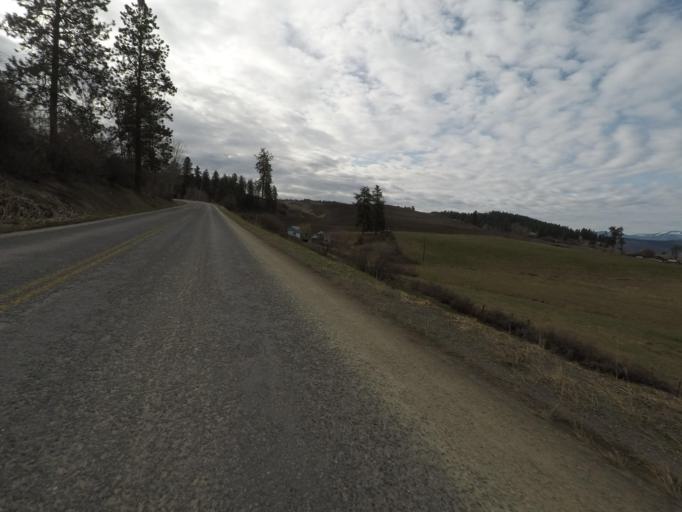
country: US
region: Washington
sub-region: Stevens County
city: Colville
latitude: 48.5201
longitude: -117.8795
